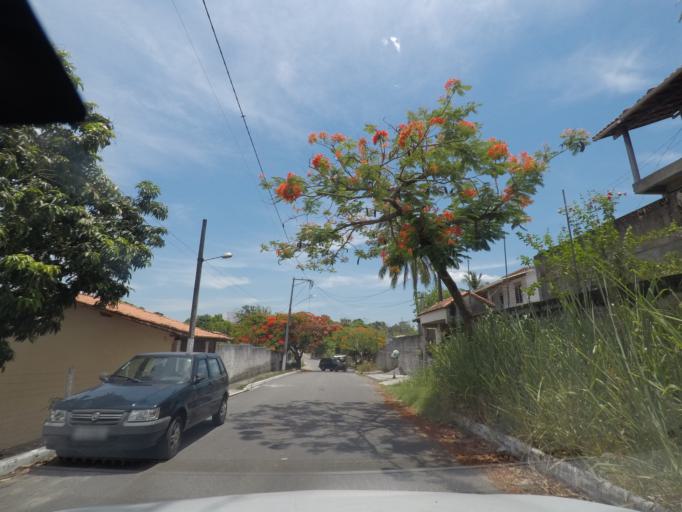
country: BR
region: Rio de Janeiro
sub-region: Marica
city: Marica
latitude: -22.9288
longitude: -42.8242
